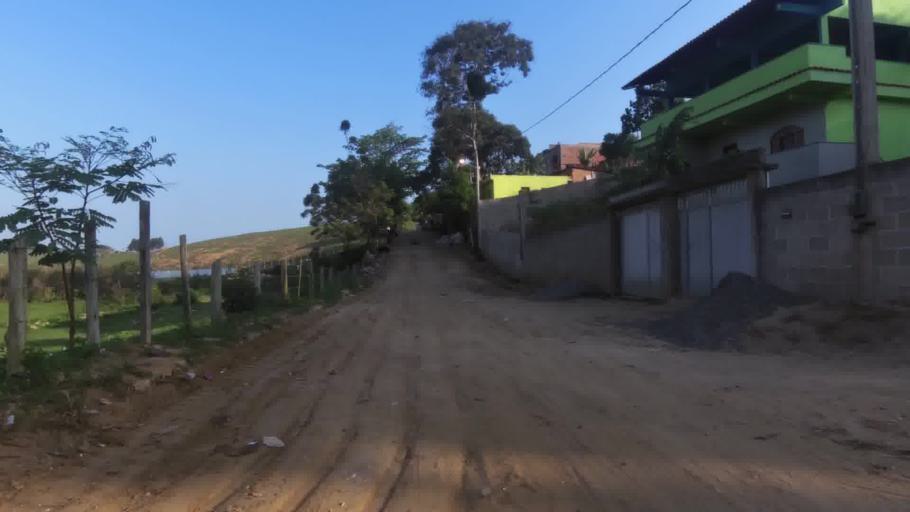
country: BR
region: Espirito Santo
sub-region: Piuma
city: Piuma
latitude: -20.8247
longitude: -40.7187
